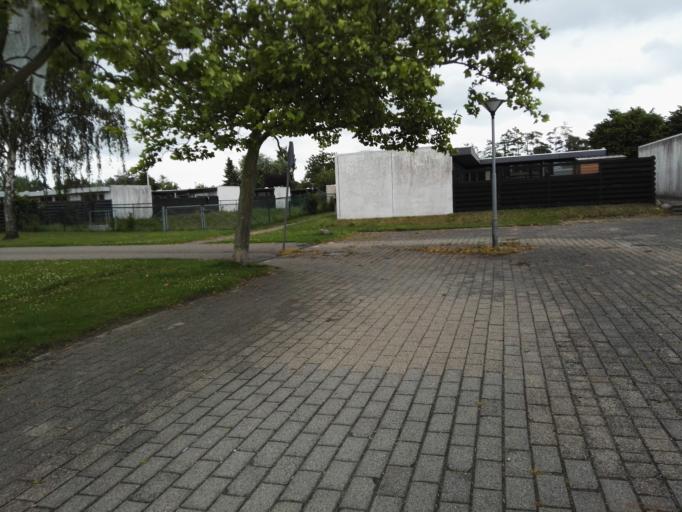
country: DK
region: Capital Region
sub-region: Egedal Kommune
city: Olstykke
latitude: 55.7857
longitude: 12.1728
